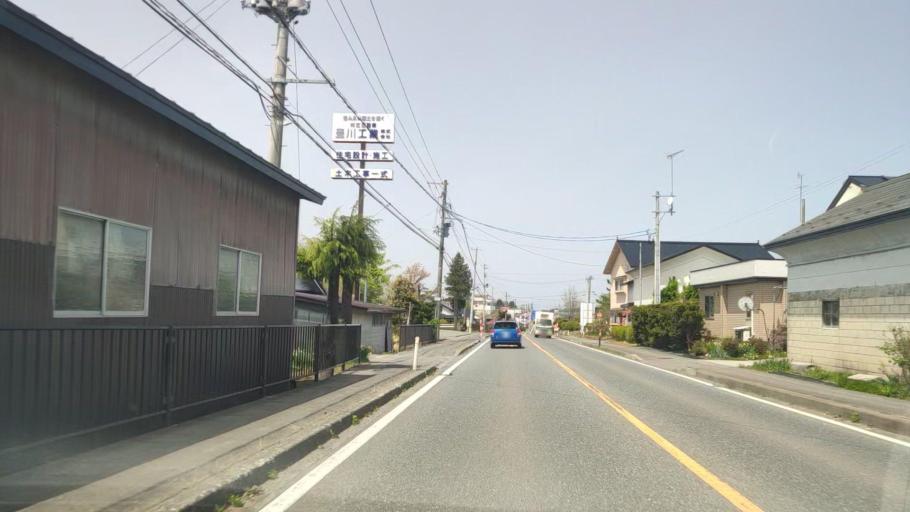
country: JP
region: Aomori
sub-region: Misawa Shi
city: Inuotose
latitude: 40.6533
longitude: 141.1944
